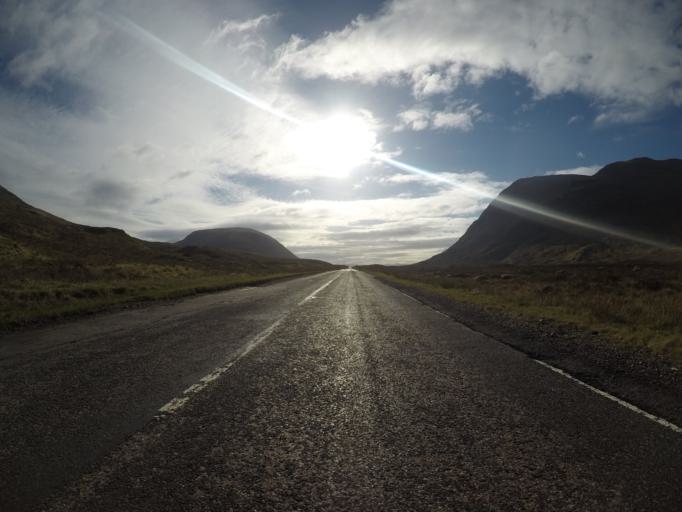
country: GB
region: Scotland
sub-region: Highland
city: Spean Bridge
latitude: 56.6627
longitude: -4.9287
